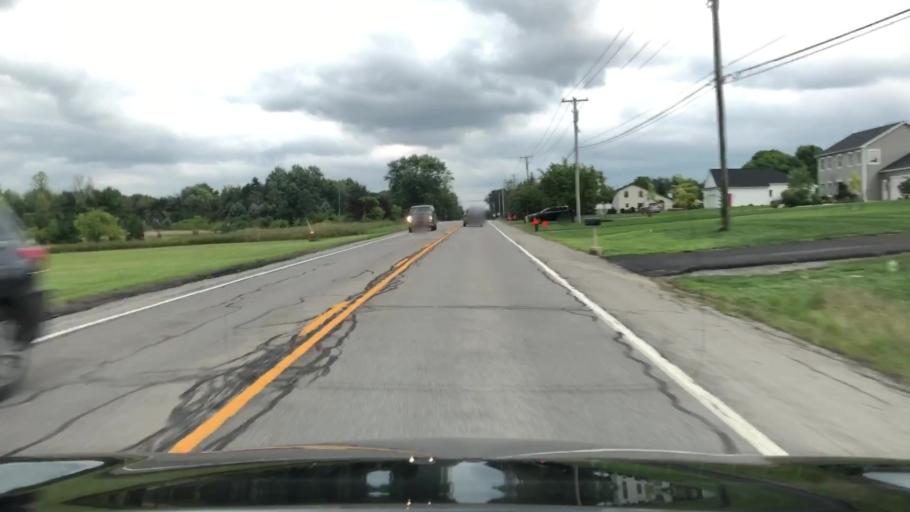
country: US
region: New York
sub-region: Erie County
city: Orchard Park
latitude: 42.7916
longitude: -78.6969
